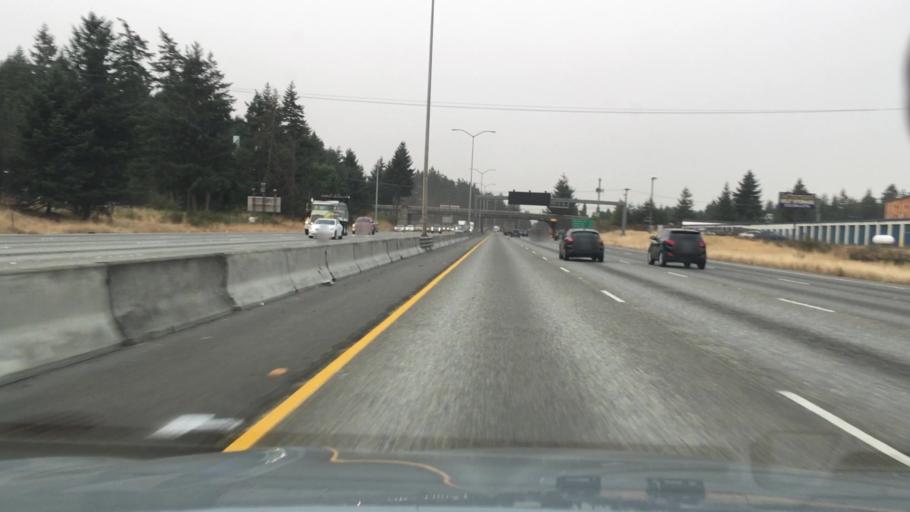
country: US
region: Washington
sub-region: Pierce County
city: McChord Air Force Base
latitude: 47.1429
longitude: -122.5125
